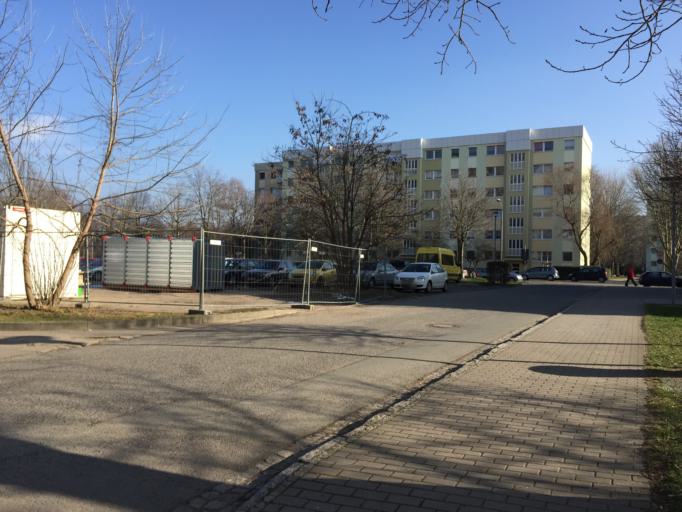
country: DE
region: Saxony
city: Dresden
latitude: 51.0368
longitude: 13.7358
